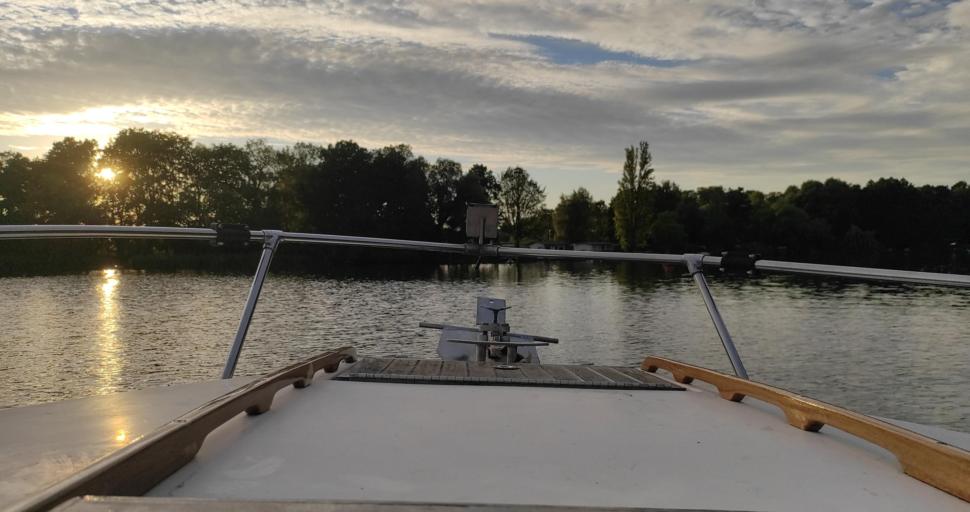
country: DE
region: Brandenburg
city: Friedland
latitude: 52.0233
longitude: 14.1801
